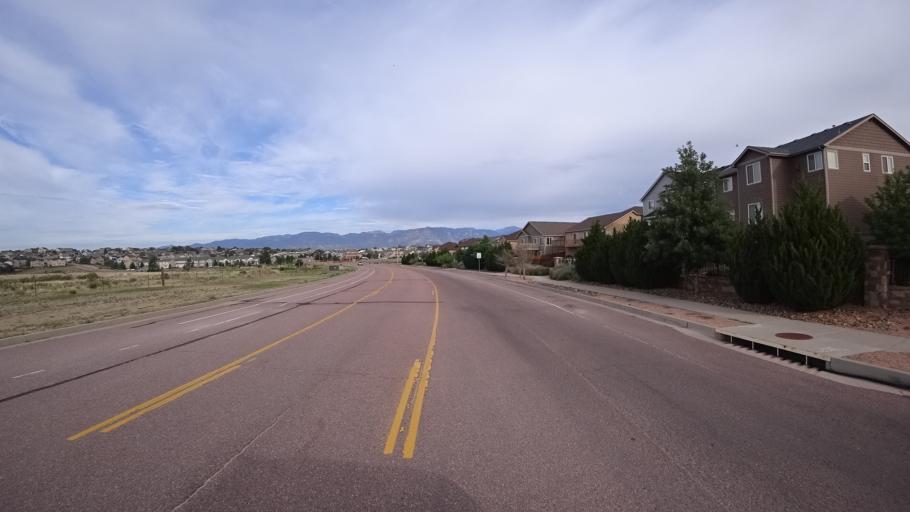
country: US
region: Colorado
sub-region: El Paso County
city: Fountain
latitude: 38.7153
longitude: -104.6837
